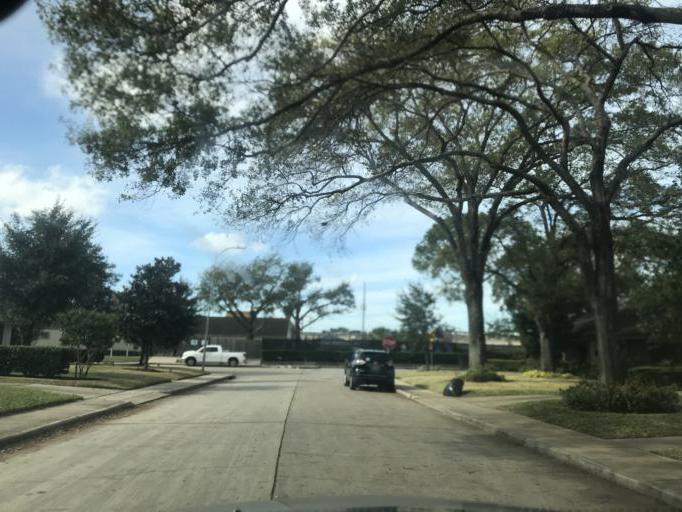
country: US
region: Texas
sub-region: Harris County
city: Piney Point Village
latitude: 29.7386
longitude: -95.4947
